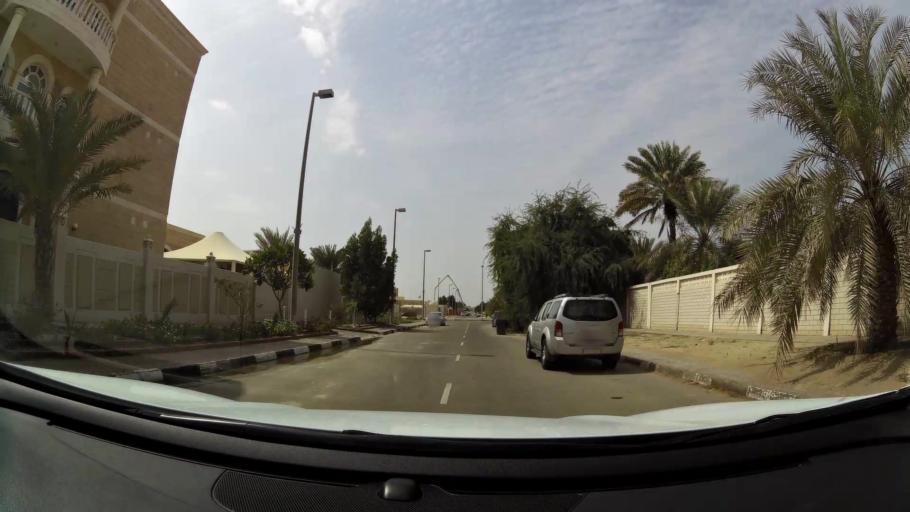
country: AE
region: Abu Dhabi
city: Abu Dhabi
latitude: 24.5312
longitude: 54.6894
